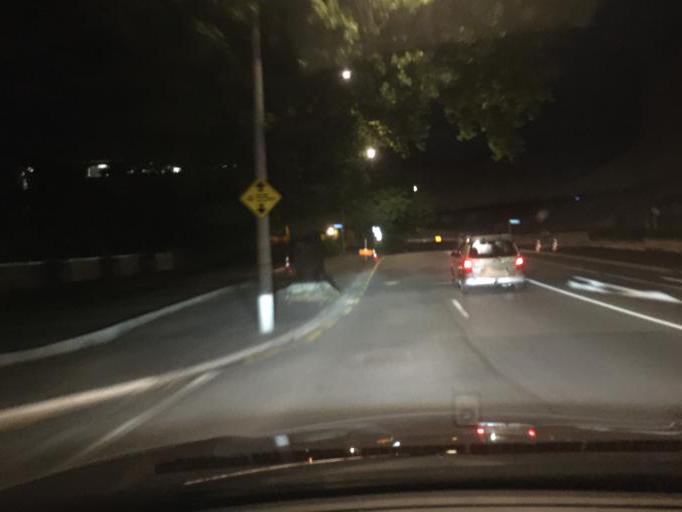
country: NZ
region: Waikato
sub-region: Hamilton City
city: Hamilton
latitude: -37.7885
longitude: 175.2773
